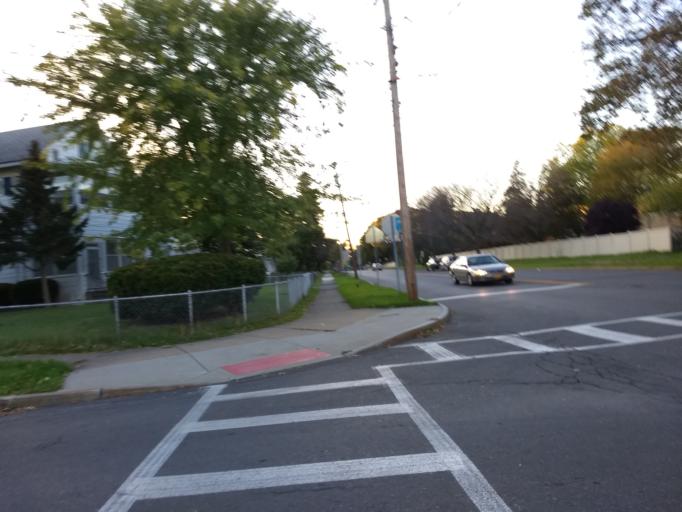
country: US
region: New York
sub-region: Onondaga County
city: Mattydale
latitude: 43.0739
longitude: -76.1498
